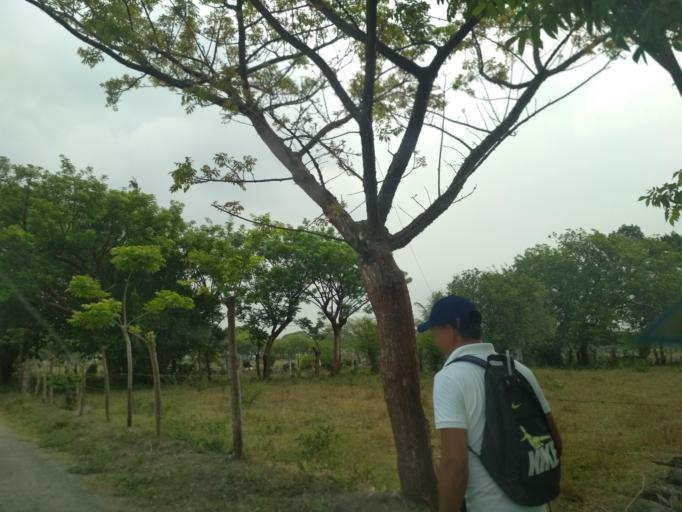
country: MX
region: Veracruz
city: Paso del Toro
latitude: 19.0180
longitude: -96.1502
